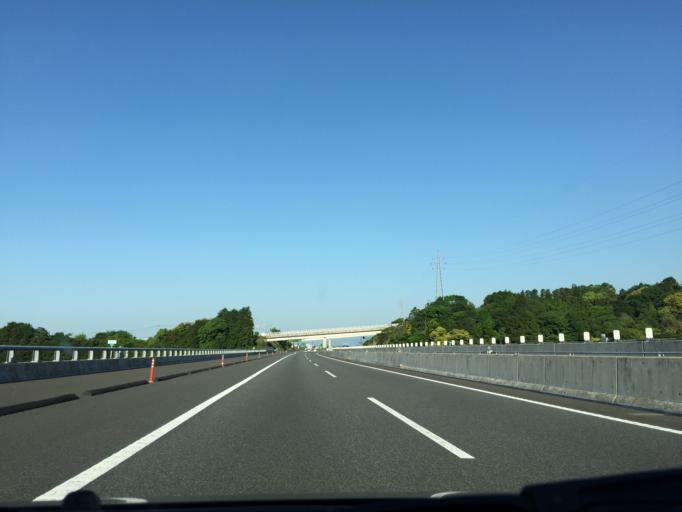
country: JP
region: Shizuoka
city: Numazu
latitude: 35.1539
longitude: 138.8187
